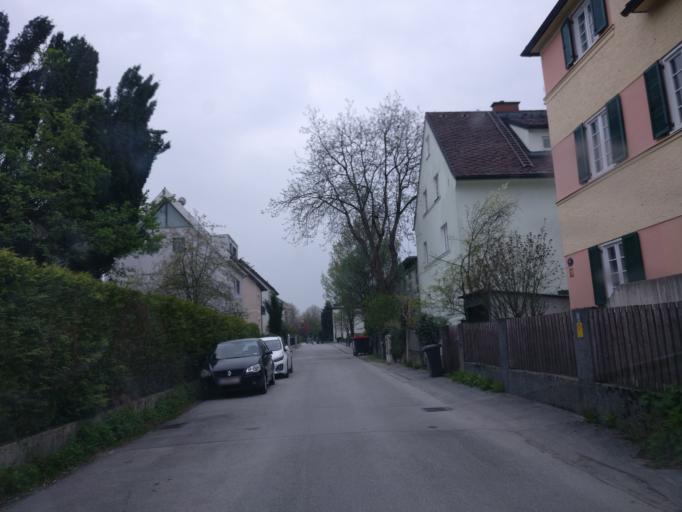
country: AT
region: Salzburg
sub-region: Politischer Bezirk Salzburg-Umgebung
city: Bergheim
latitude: 47.8173
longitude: 13.0377
